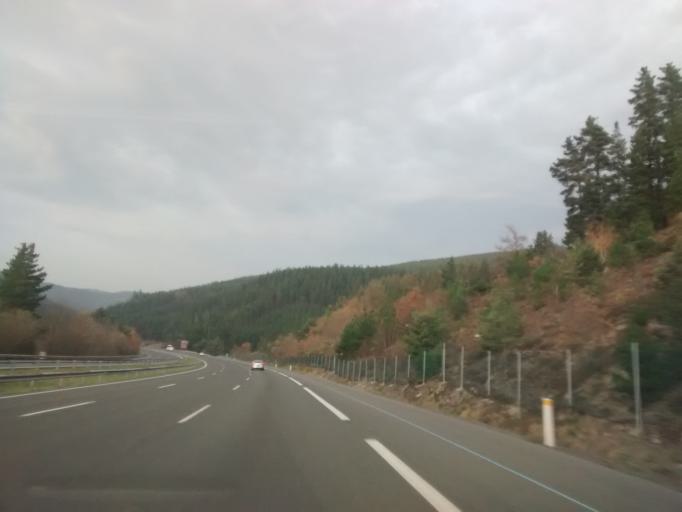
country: ES
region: Basque Country
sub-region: Provincia de Alava
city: Lezama
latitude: 43.0295
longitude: -2.9117
